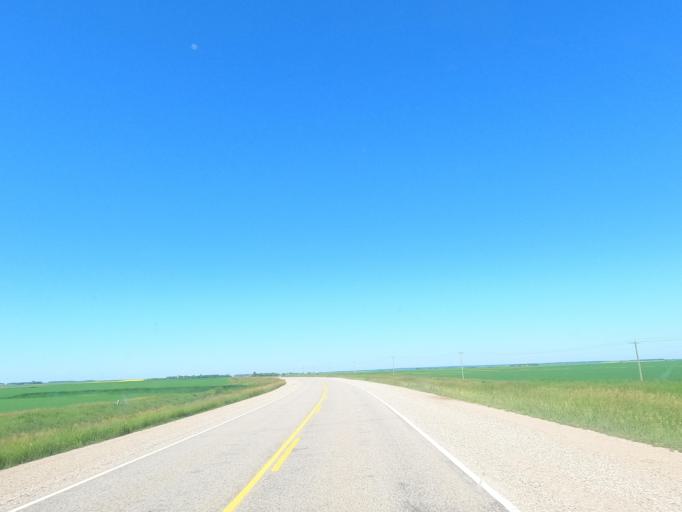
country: CA
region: Manitoba
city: Brandon
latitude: 49.5908
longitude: -99.7591
